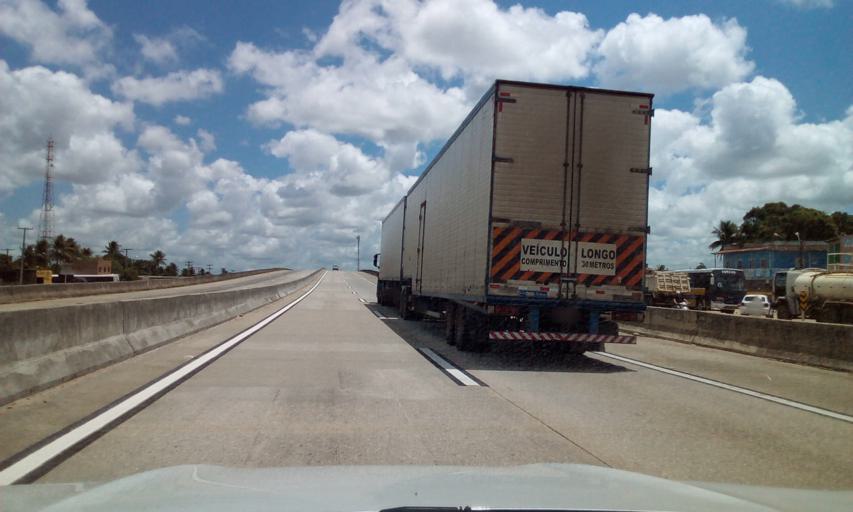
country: BR
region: Alagoas
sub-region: Campo Alegre
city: Campo Alegre
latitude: -9.9056
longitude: -36.3535
